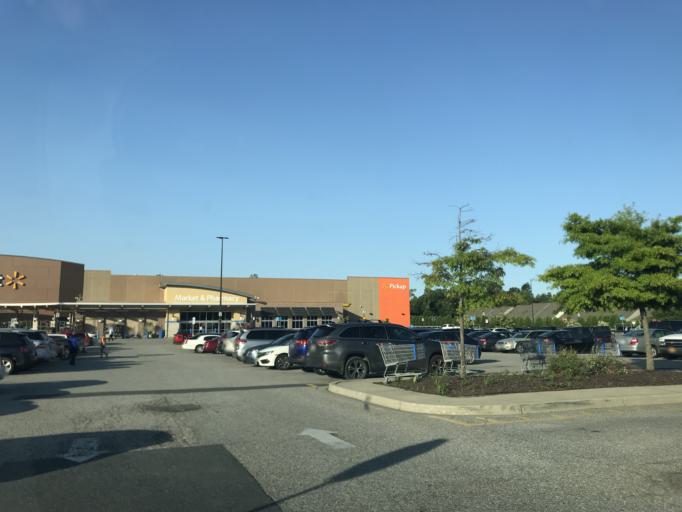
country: US
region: Maryland
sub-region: Harford County
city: Pleasant Hills
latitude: 39.4974
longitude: -76.3858
